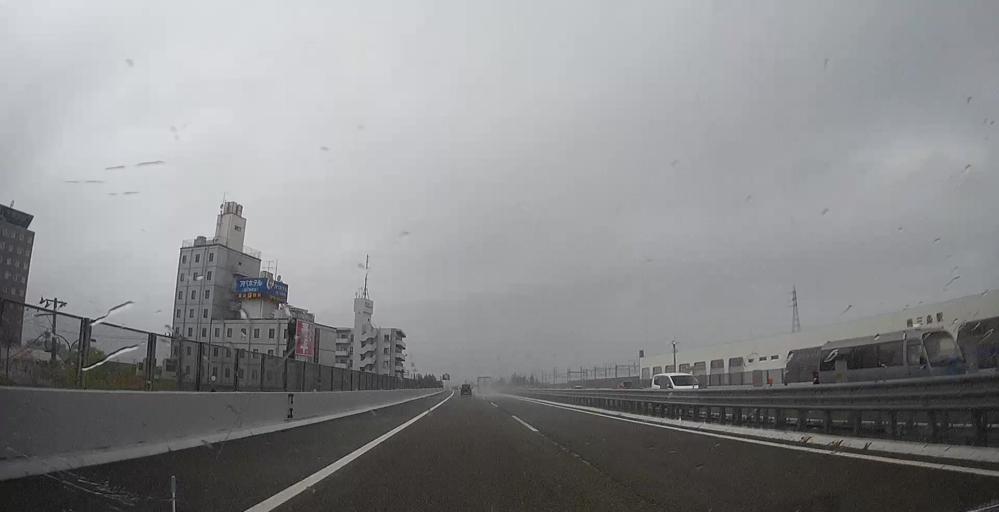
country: JP
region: Niigata
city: Tsubame
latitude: 37.6480
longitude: 138.9373
